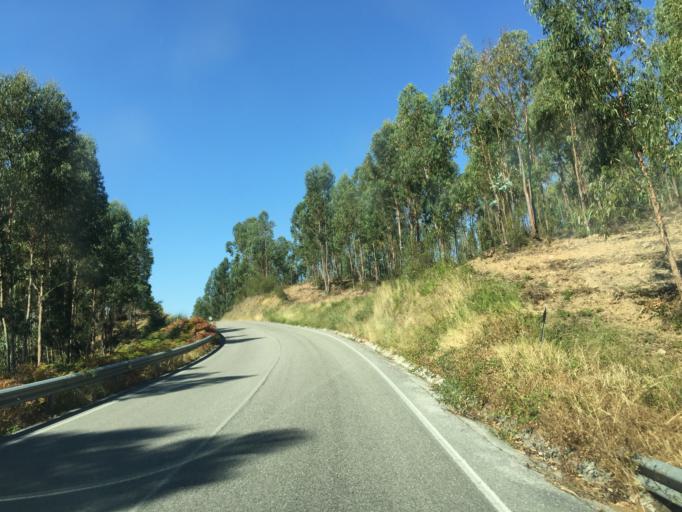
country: PT
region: Santarem
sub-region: Tomar
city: Tomar
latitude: 39.6086
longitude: -8.3402
